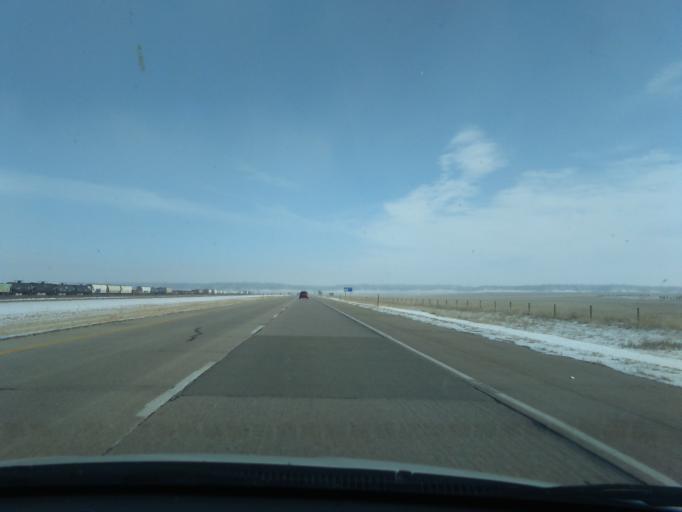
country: US
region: Wyoming
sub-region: Laramie County
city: Pine Bluffs
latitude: 41.1487
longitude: -104.1368
